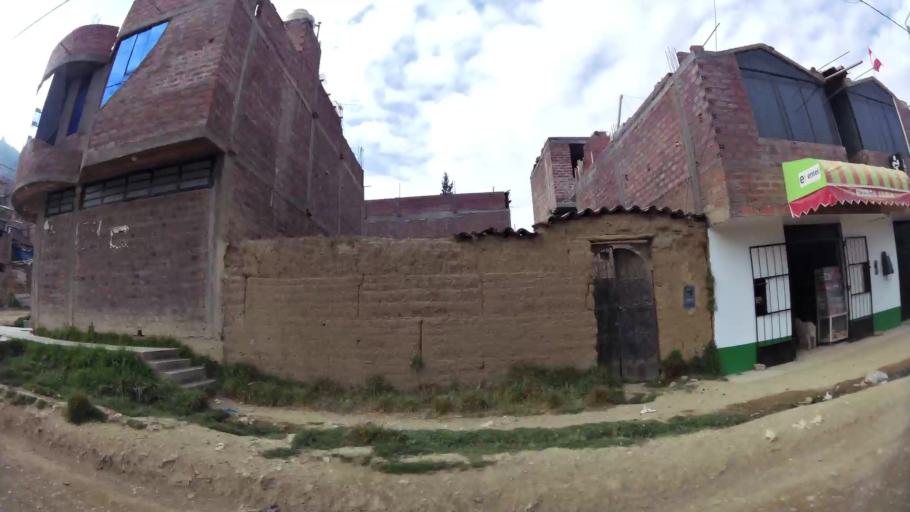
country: PE
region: Junin
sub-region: Provincia de Huancayo
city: Huancayo
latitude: -12.0531
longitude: -75.1864
